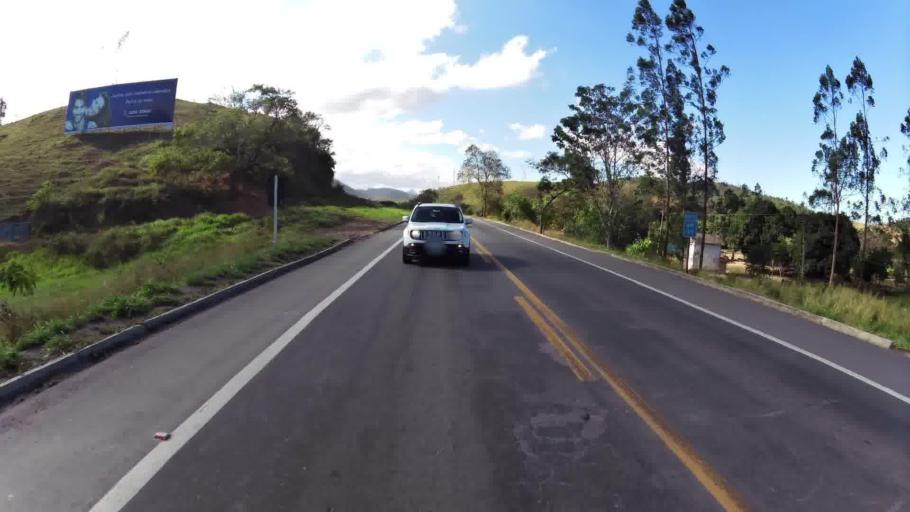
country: BR
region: Espirito Santo
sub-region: Viana
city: Viana
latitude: -20.4345
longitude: -40.4596
